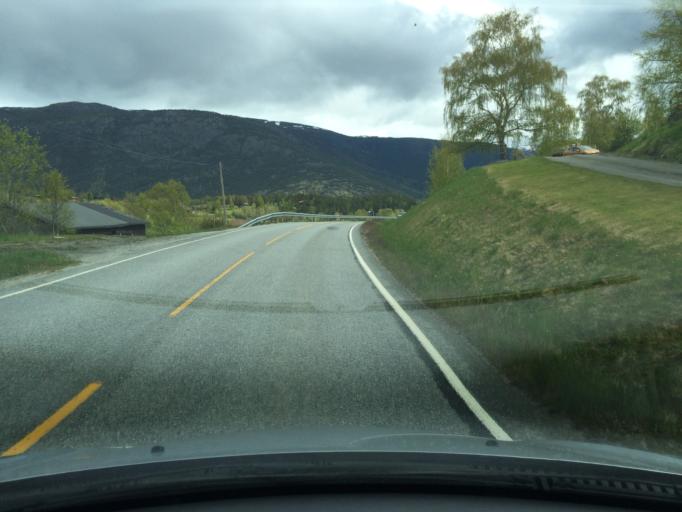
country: NO
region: Oppland
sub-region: Lom
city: Fossbergom
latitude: 61.8298
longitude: 8.5516
